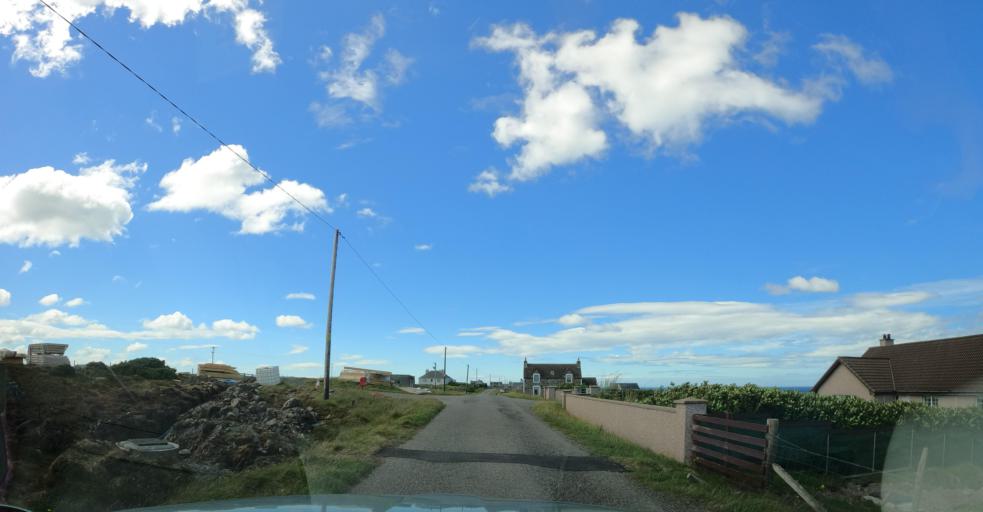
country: GB
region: Scotland
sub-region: Eilean Siar
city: Isle of Lewis
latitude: 58.3561
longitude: -6.5539
